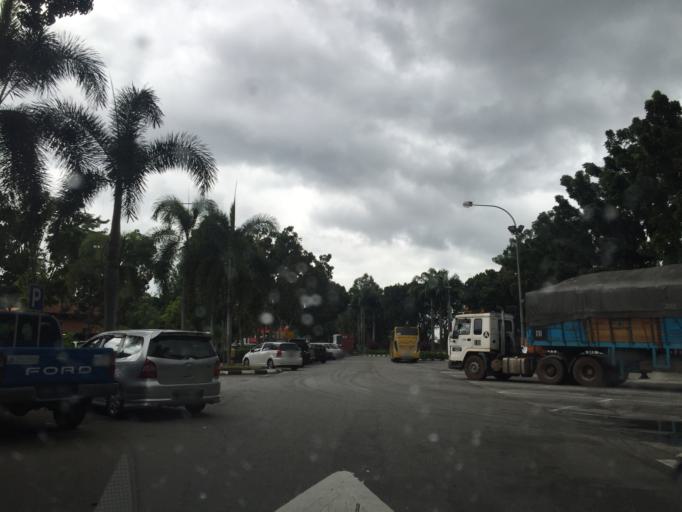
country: MY
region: Perak
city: Taiping
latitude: 4.7730
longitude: 100.7629
